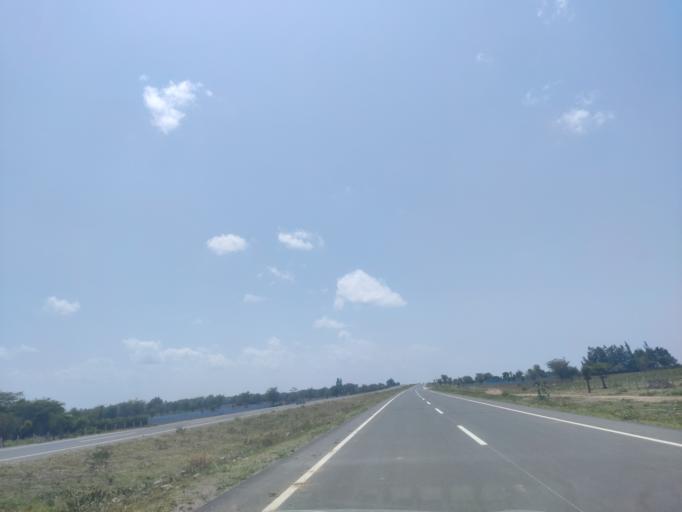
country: ET
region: Oromiya
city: Mojo
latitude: 8.3406
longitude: 38.9720
